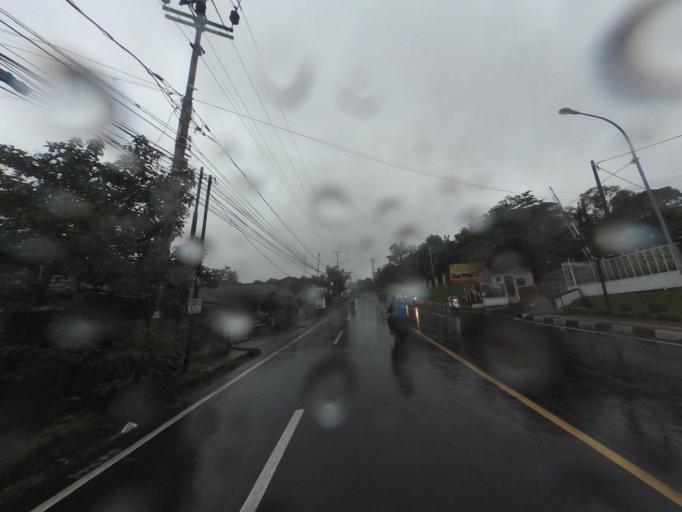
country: ID
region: West Java
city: Caringin
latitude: -6.6537
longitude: 106.8733
